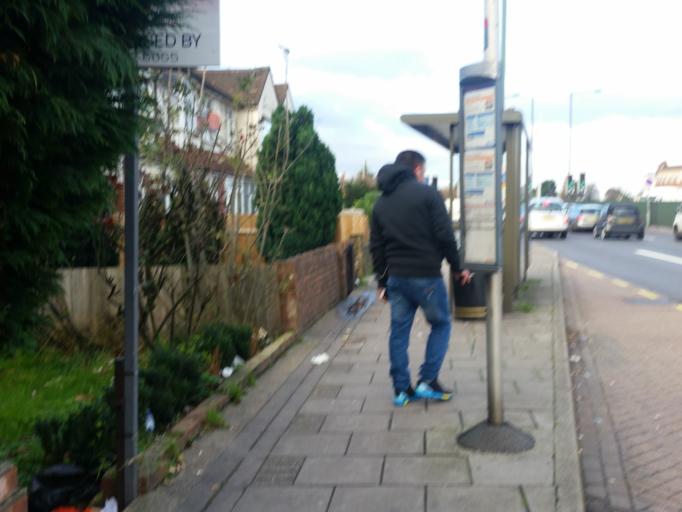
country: GB
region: England
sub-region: Greater London
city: Wood Green
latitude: 51.6152
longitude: -0.0870
